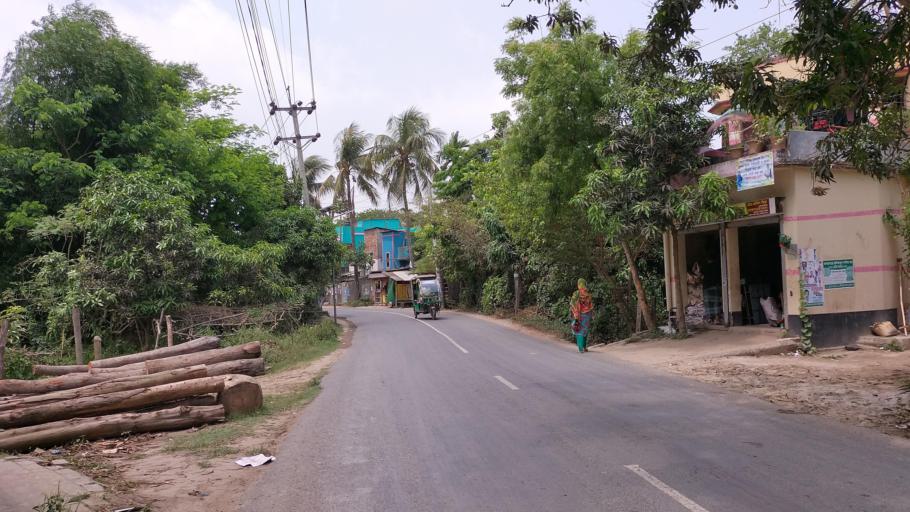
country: BD
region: Dhaka
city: Azimpur
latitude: 23.7296
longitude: 90.2845
